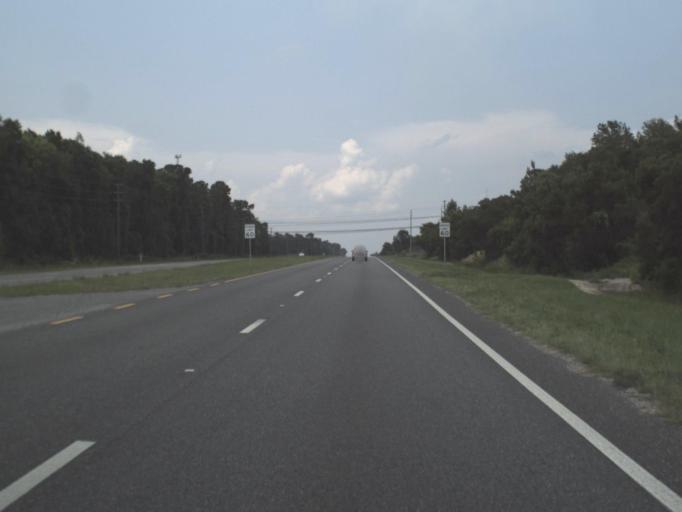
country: US
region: Florida
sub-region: Putnam County
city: Palatka
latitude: 29.7227
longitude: -81.6538
